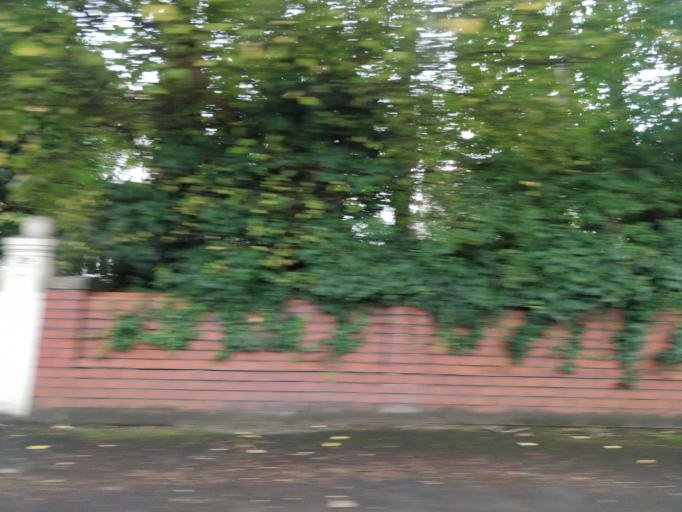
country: GB
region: England
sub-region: Sefton
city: Southport
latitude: 53.6598
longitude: -2.9780
